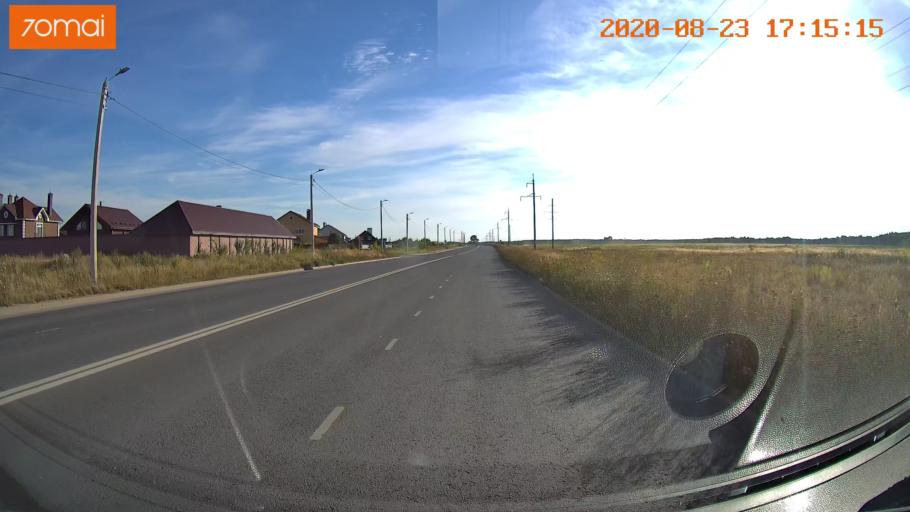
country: RU
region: Ivanovo
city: Novo-Talitsy
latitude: 57.0464
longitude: 40.9143
